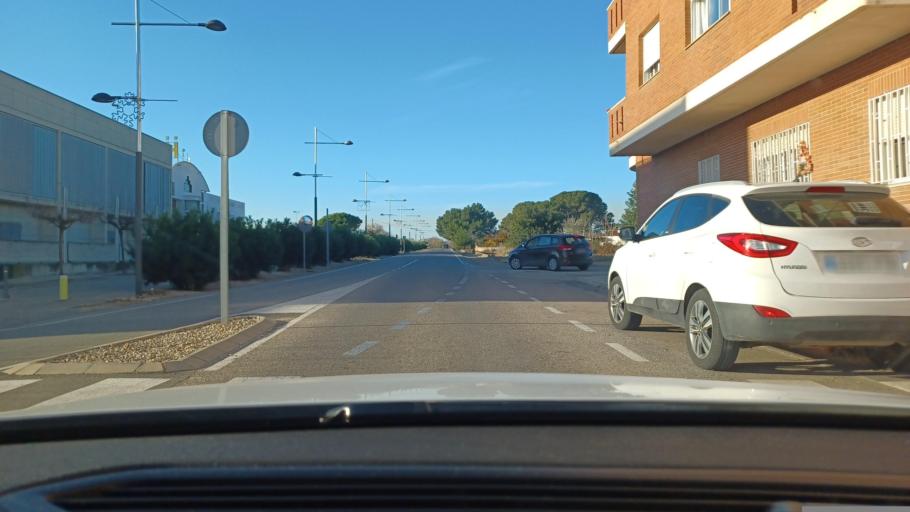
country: ES
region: Catalonia
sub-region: Provincia de Tarragona
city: Santa Barbara
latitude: 40.7130
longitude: 0.4886
